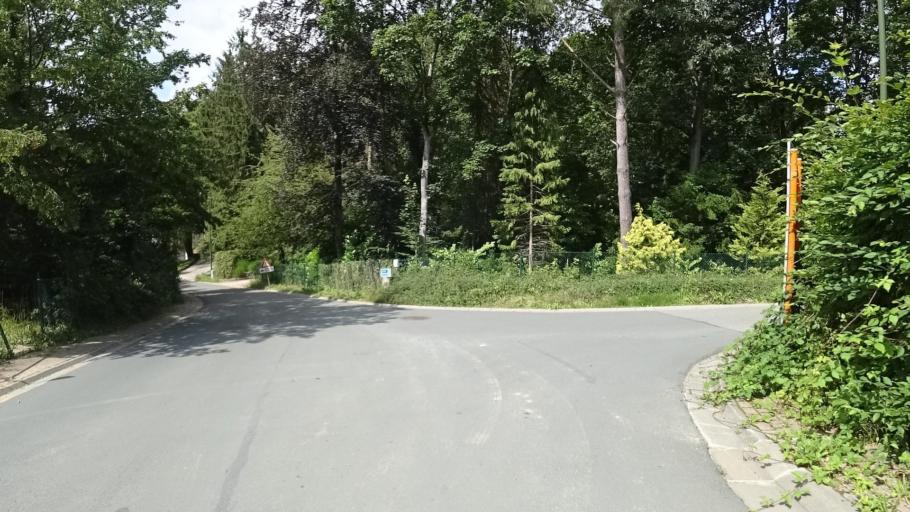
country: BE
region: Wallonia
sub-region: Province du Brabant Wallon
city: Villers-la-Ville
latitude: 50.5784
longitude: 4.5394
